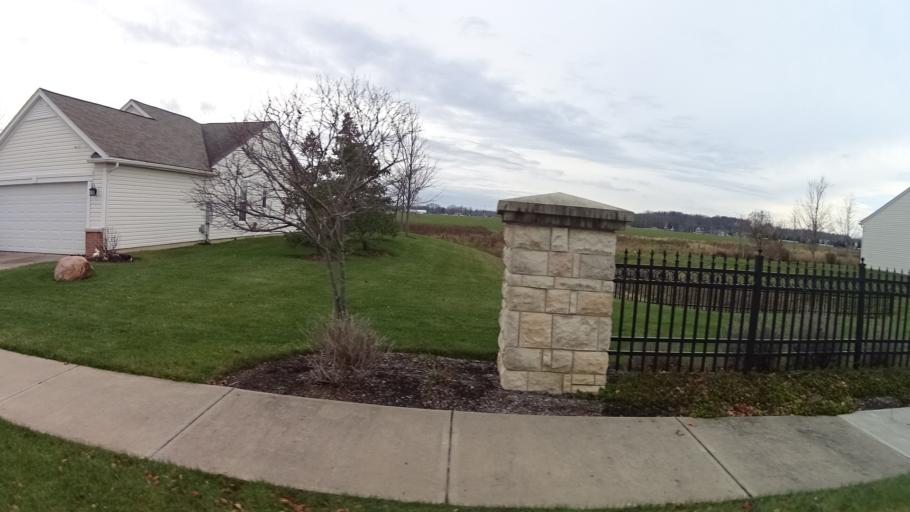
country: US
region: Ohio
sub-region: Lorain County
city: North Ridgeville
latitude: 41.3522
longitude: -82.0534
